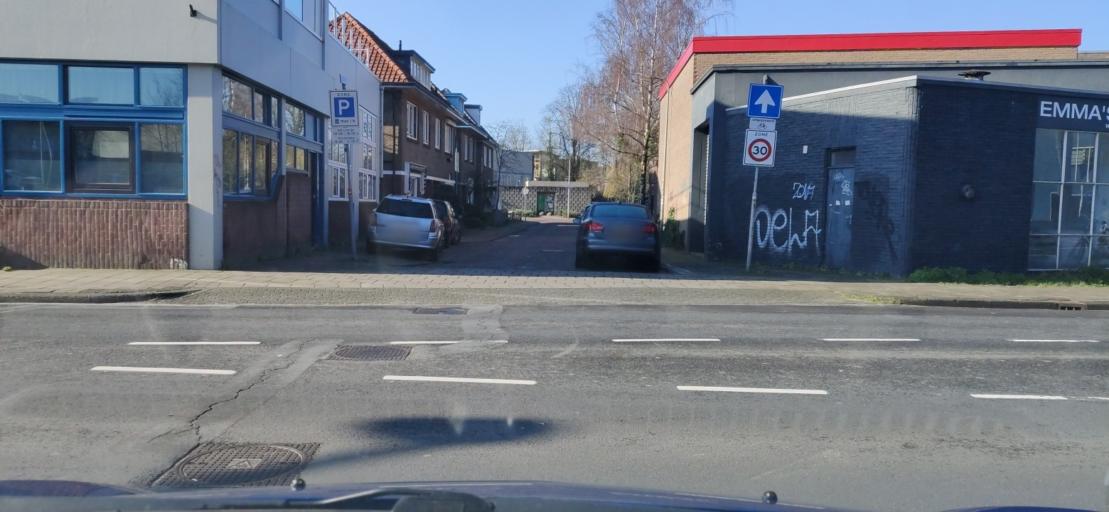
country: NL
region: Overijssel
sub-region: Gemeente Hengelo
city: Hengelo
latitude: 52.2644
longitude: 6.7896
